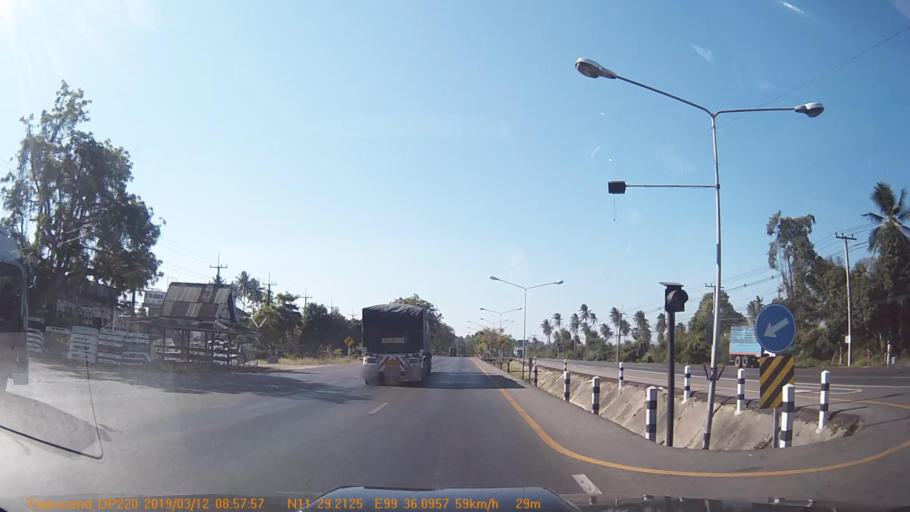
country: TH
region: Prachuap Khiri Khan
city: Thap Sakae
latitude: 11.4867
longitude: 99.6016
